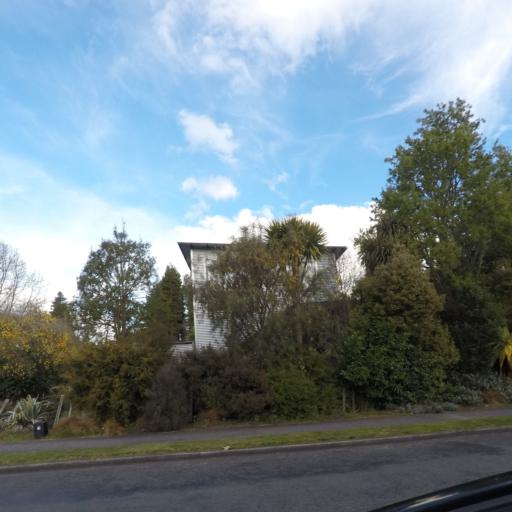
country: NZ
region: Manawatu-Wanganui
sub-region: Ruapehu District
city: Waiouru
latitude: -39.4028
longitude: 175.4115
